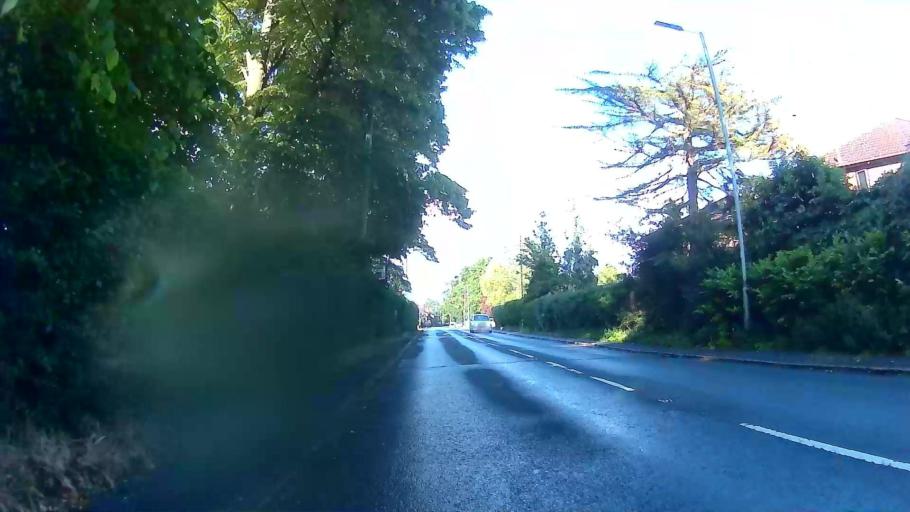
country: GB
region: England
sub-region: Essex
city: Writtle
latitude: 51.7292
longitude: 0.4126
